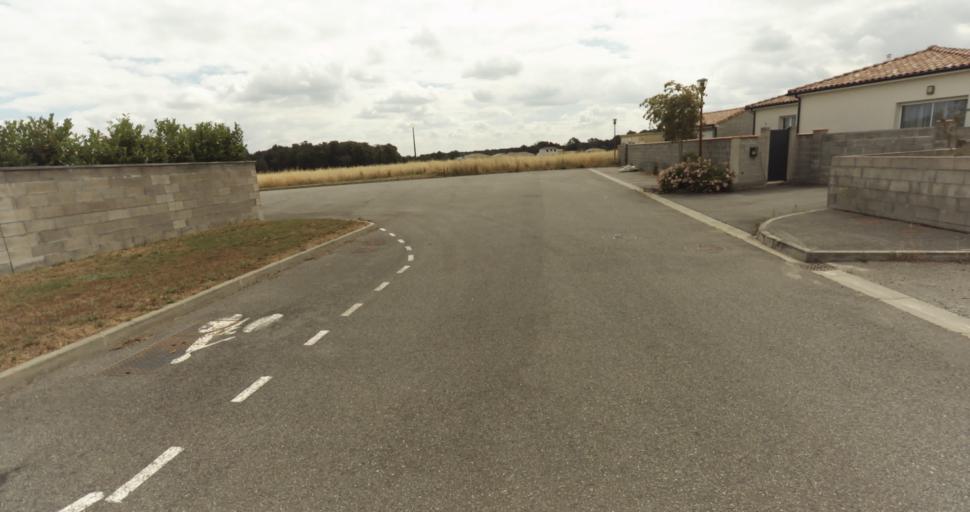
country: FR
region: Midi-Pyrenees
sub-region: Departement de la Haute-Garonne
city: Fontenilles
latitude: 43.5560
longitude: 1.2013
